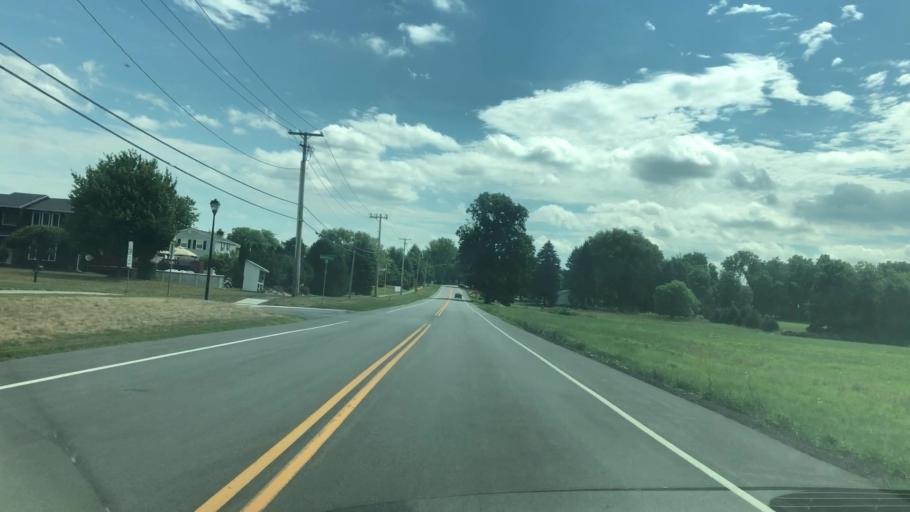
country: US
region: New York
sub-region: Monroe County
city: Fairport
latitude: 43.0794
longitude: -77.3971
